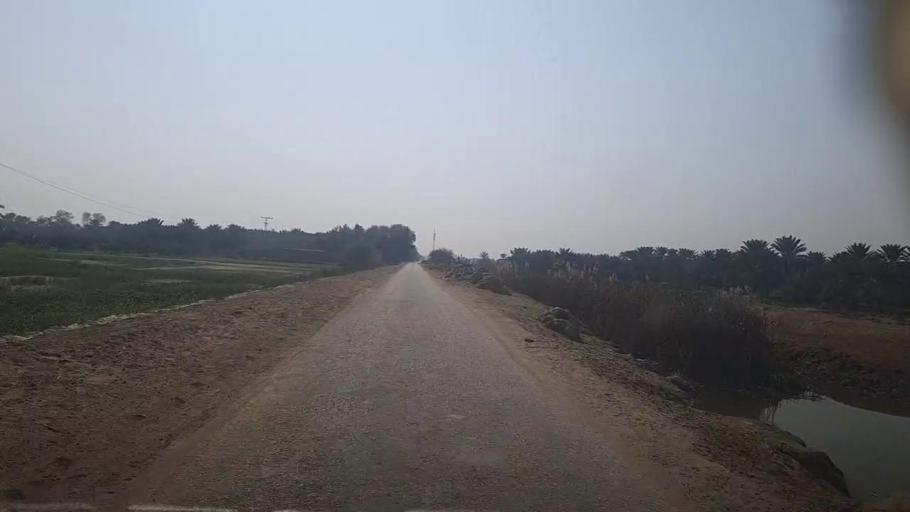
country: PK
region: Sindh
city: Khairpur
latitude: 27.4524
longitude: 68.8126
